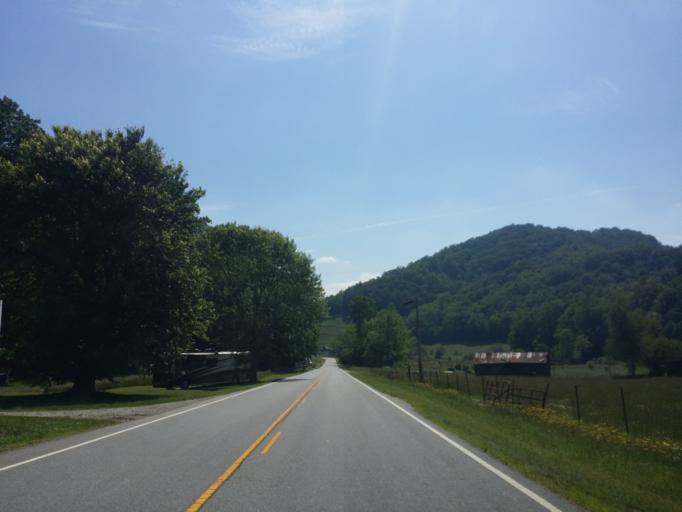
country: US
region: North Carolina
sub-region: Madison County
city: Marshall
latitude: 35.7003
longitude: -82.8099
